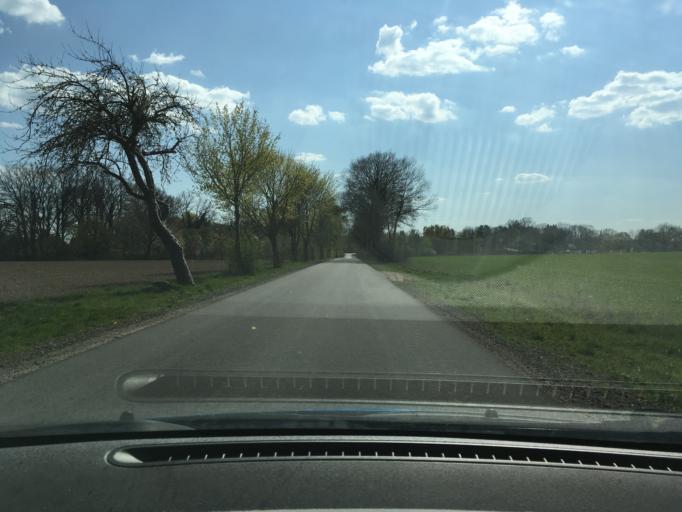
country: DE
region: Lower Saxony
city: Reinstorf
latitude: 53.2061
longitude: 10.5838
